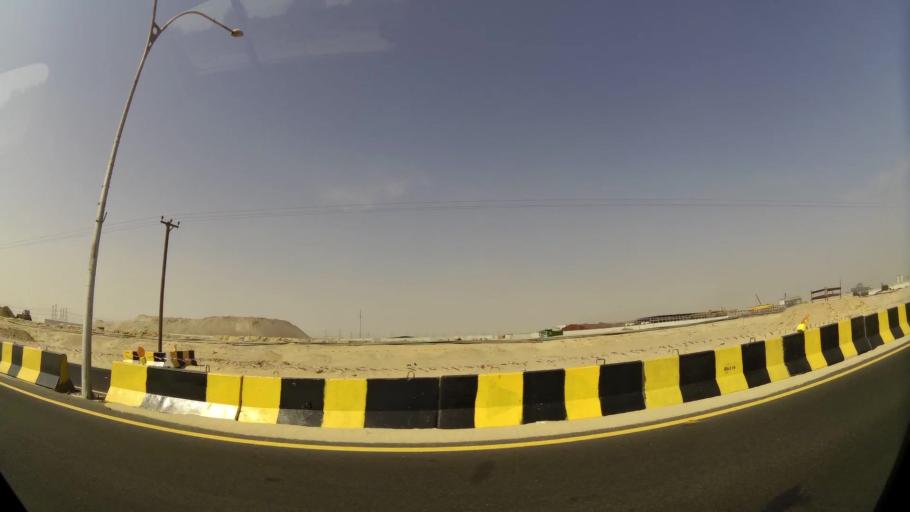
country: KW
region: Al Ahmadi
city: Al Fahahil
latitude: 28.9755
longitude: 48.1307
